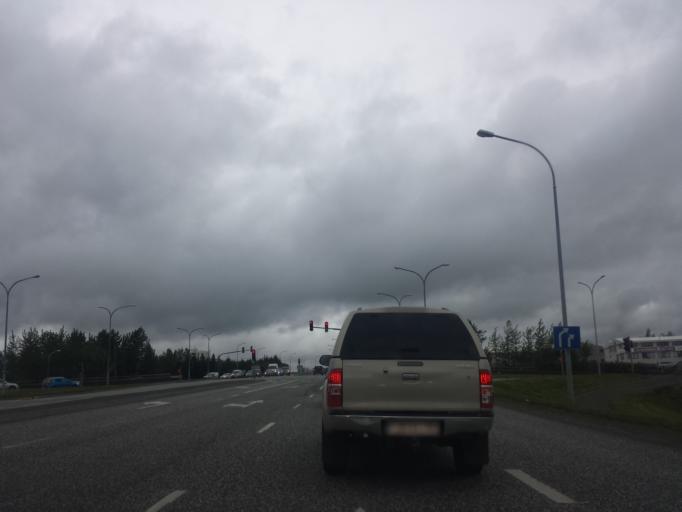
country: IS
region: Capital Region
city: Reykjavik
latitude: 64.1250
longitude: -21.8121
